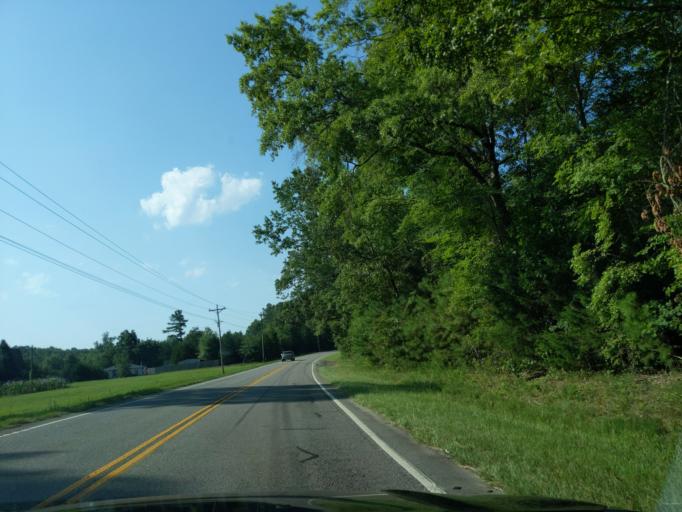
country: US
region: South Carolina
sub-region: Newberry County
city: Prosperity
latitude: 34.0766
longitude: -81.5601
